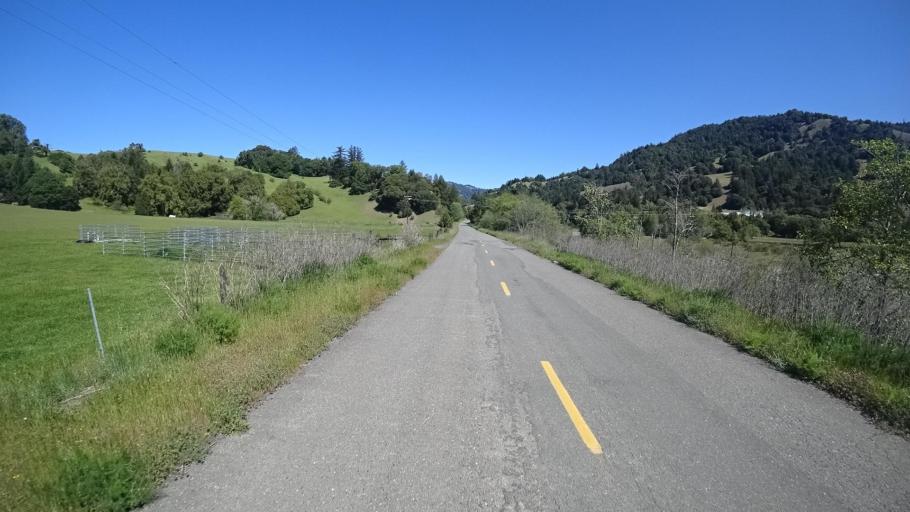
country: US
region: California
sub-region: Humboldt County
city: Rio Dell
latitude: 40.2384
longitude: -124.1213
